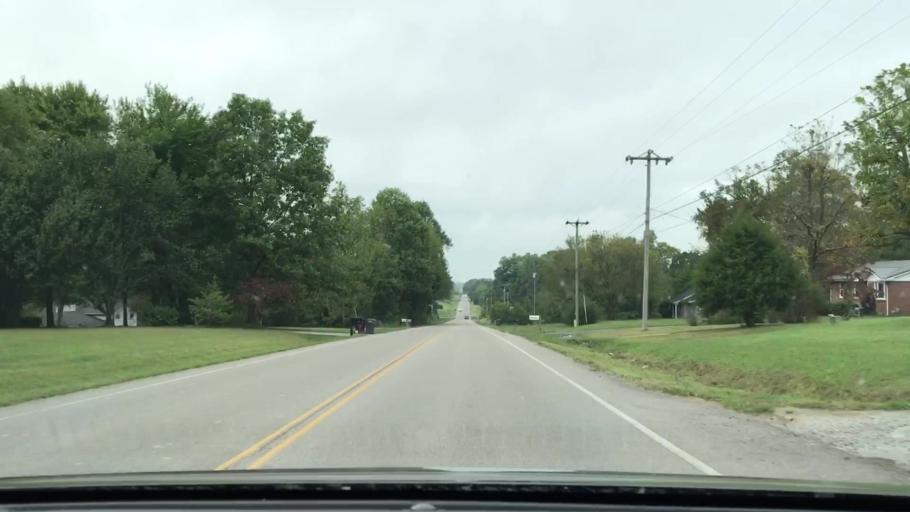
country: US
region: Tennessee
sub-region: Sumner County
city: Portland
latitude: 36.5184
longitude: -86.5010
